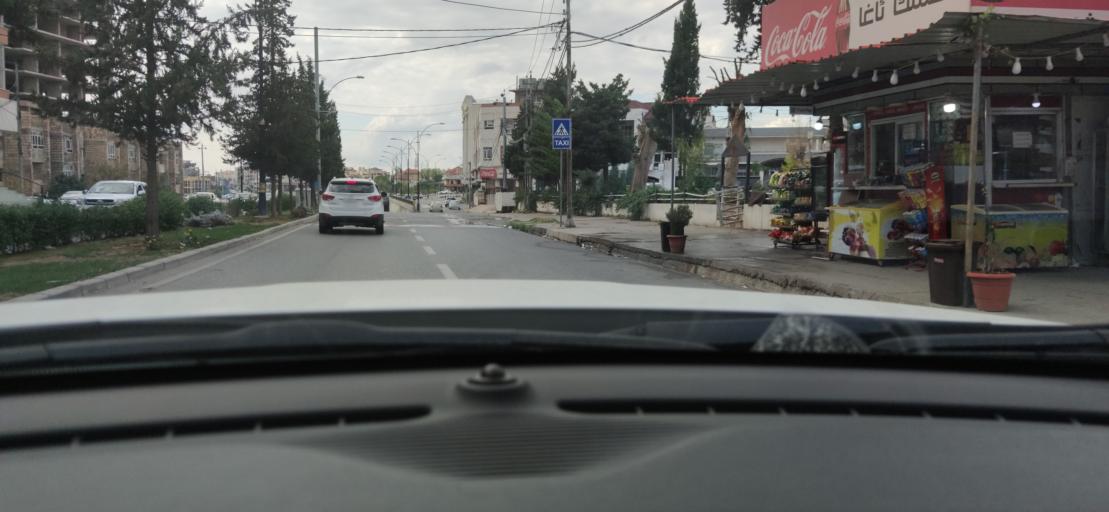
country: IQ
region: Dahuk
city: Dihok
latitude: 36.8667
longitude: 42.9812
